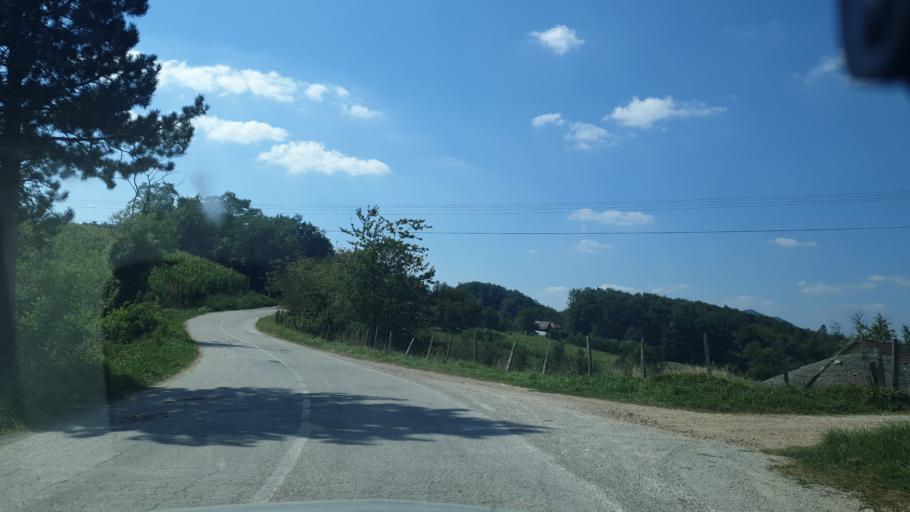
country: RS
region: Central Serbia
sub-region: Zlatiborski Okrug
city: Kosjeric
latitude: 43.9887
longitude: 20.0463
